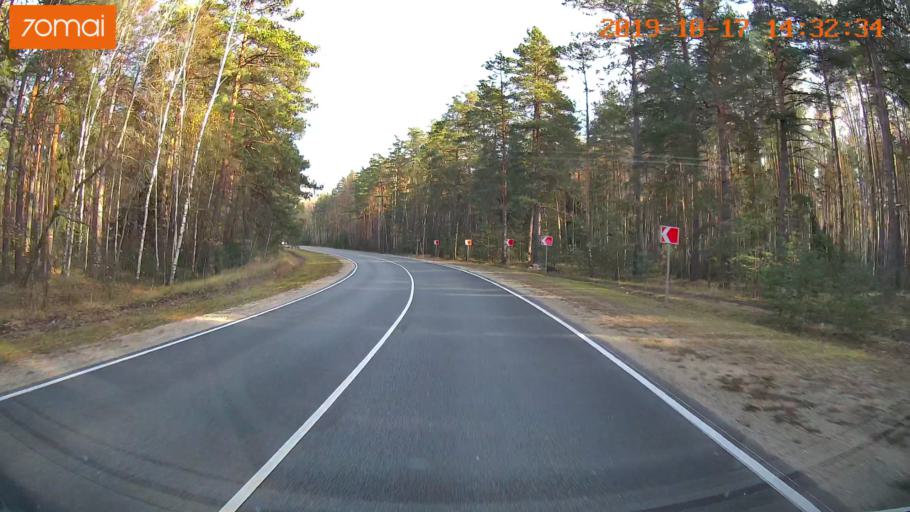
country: RU
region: Rjazan
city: Solotcha
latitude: 54.9271
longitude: 39.9813
